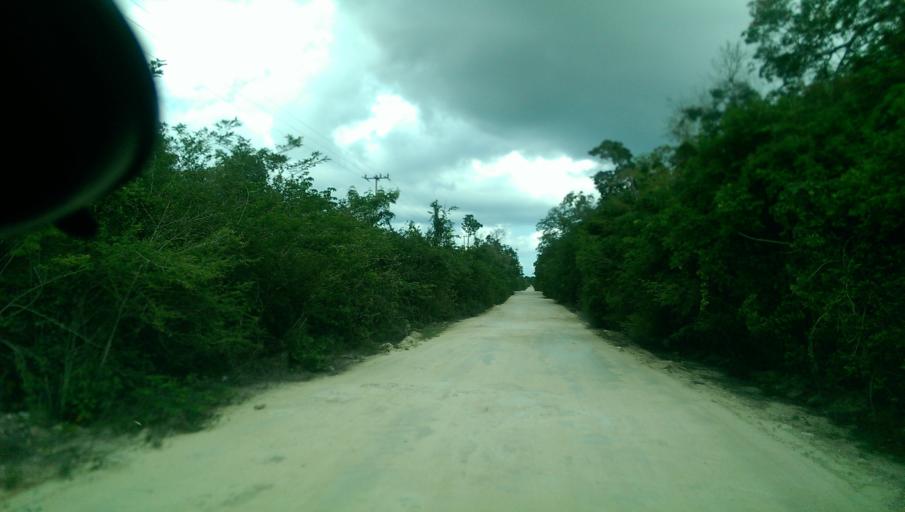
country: MX
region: Quintana Roo
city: Playa del Carmen
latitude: 20.5920
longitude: -87.1434
